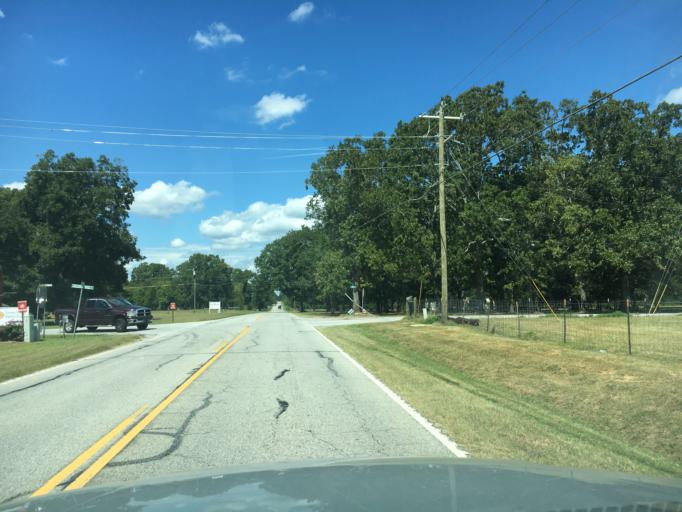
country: US
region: South Carolina
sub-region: Laurens County
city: Laurens
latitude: 34.5089
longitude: -82.0832
